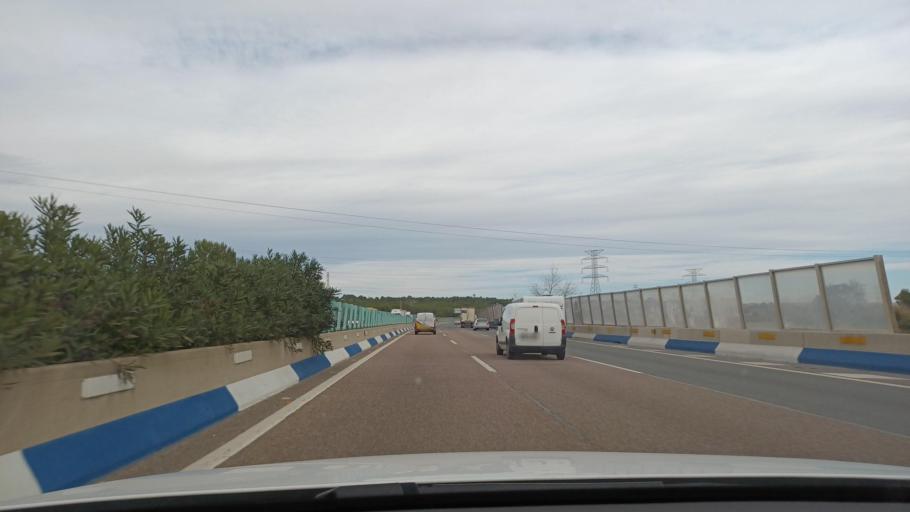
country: ES
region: Valencia
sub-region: Provincia de Valencia
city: Manises
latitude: 39.5106
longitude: -0.5037
